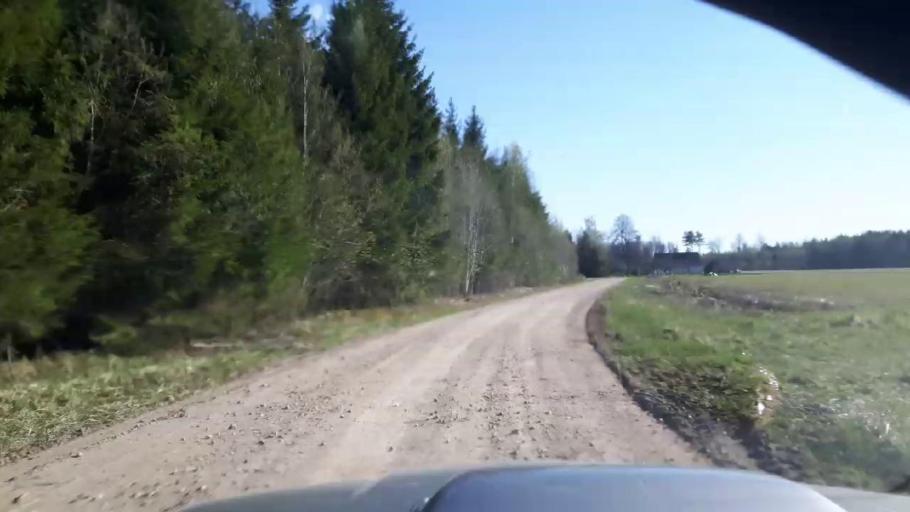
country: EE
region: Paernumaa
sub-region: Tootsi vald
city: Tootsi
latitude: 58.4307
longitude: 24.8511
